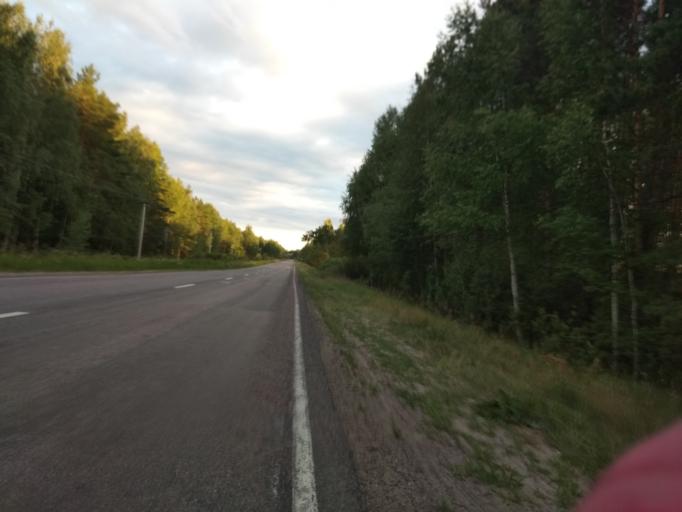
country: RU
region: Moskovskaya
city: Misheronskiy
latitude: 55.6111
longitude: 39.7170
